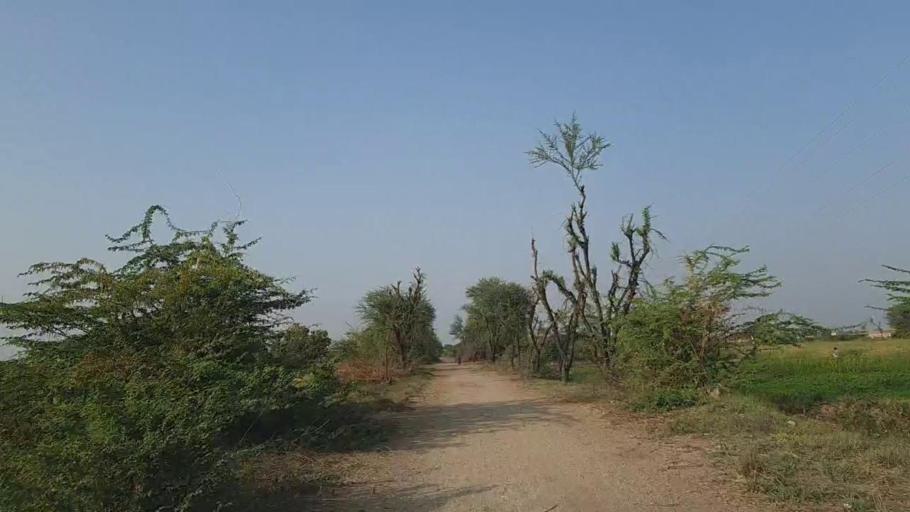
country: PK
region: Sindh
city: Dhoro Naro
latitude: 25.4951
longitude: 69.4997
